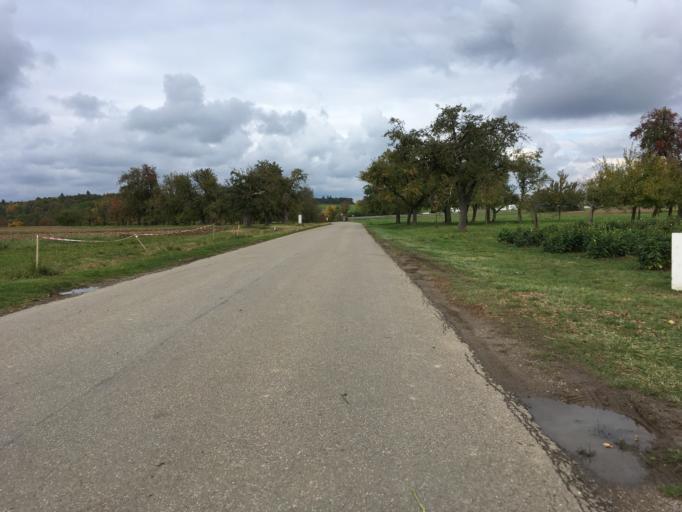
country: DE
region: Baden-Wuerttemberg
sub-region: Tuebingen Region
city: Kusterdingen
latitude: 48.5042
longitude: 9.1017
